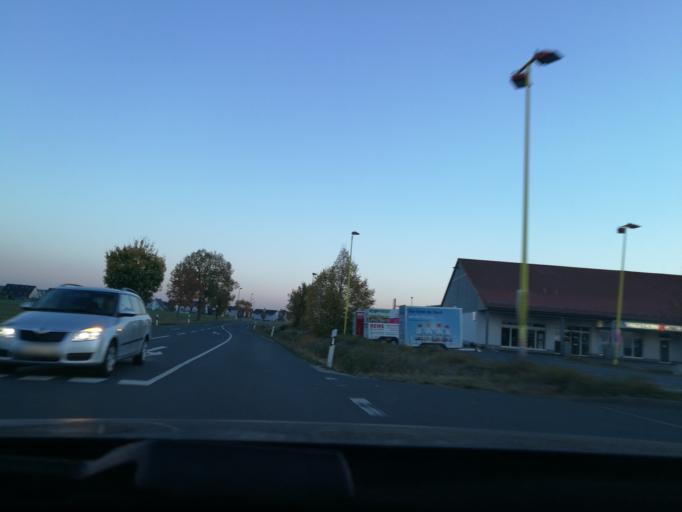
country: DE
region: Bavaria
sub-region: Regierungsbezirk Mittelfranken
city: Obermichelbach
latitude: 49.5239
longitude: 10.9050
